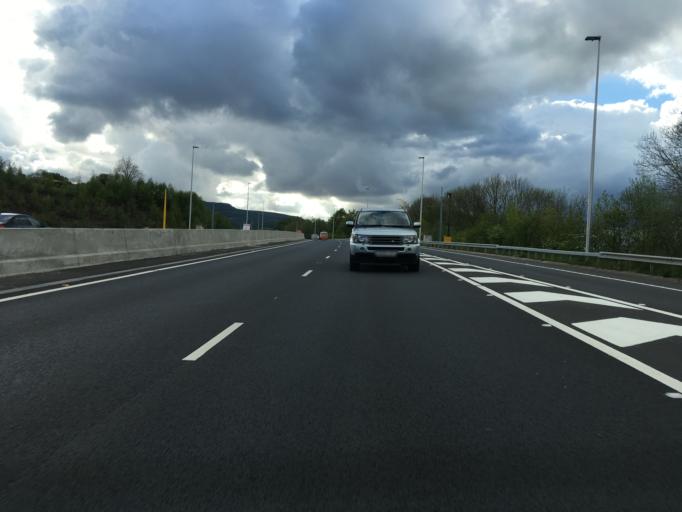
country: GB
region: Wales
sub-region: Monmouthshire
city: Gilwern
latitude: 51.8238
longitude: -3.0809
